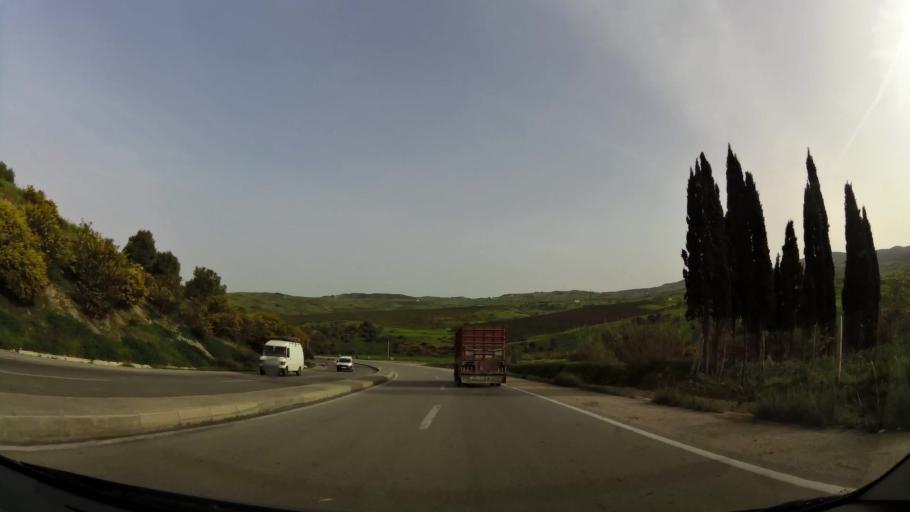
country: MA
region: Tanger-Tetouan
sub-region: Tetouan
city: Saddina
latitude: 35.5496
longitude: -5.5428
